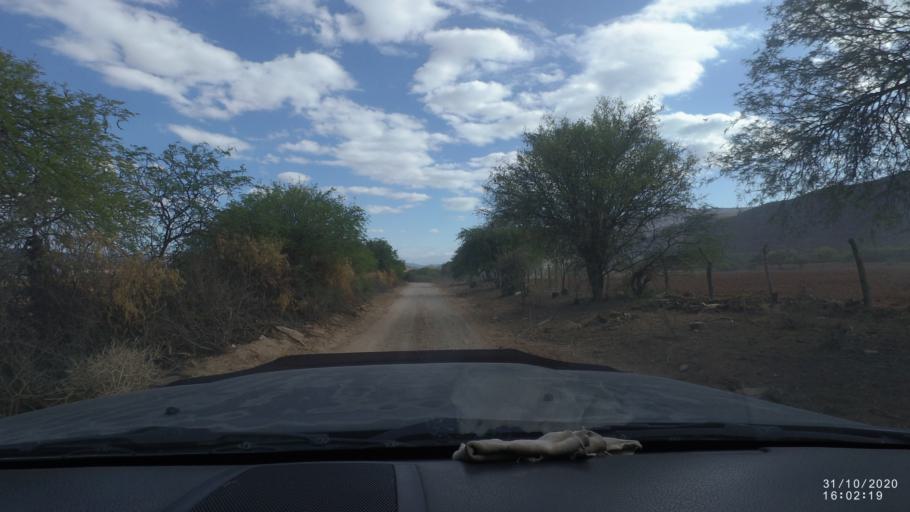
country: BO
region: Chuquisaca
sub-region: Provincia Zudanez
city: Mojocoya
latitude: -18.3460
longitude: -64.6572
